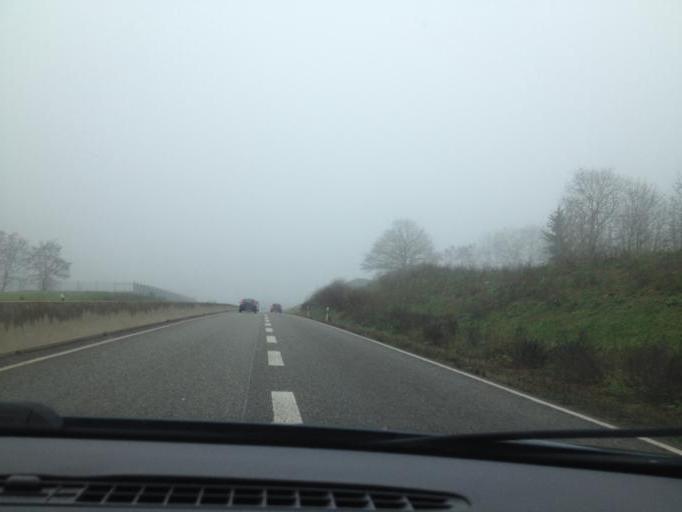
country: DE
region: Rheinland-Pfalz
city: Katzweiler
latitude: 49.4692
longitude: 7.6998
